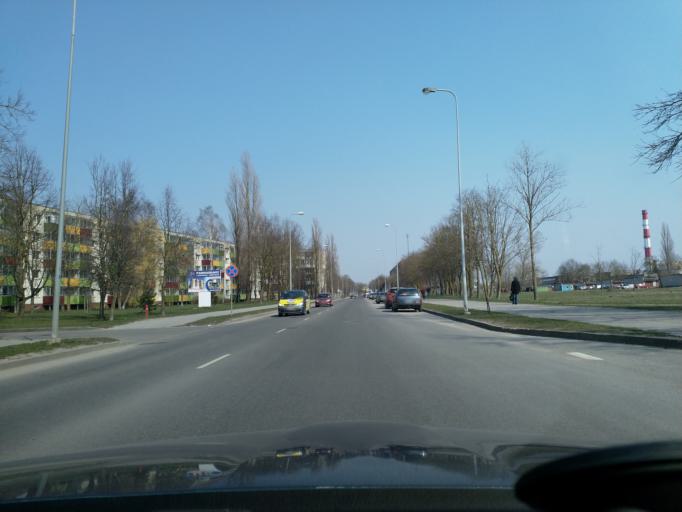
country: LT
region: Klaipedos apskritis
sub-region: Klaipeda
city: Klaipeda
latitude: 55.6958
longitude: 21.1571
